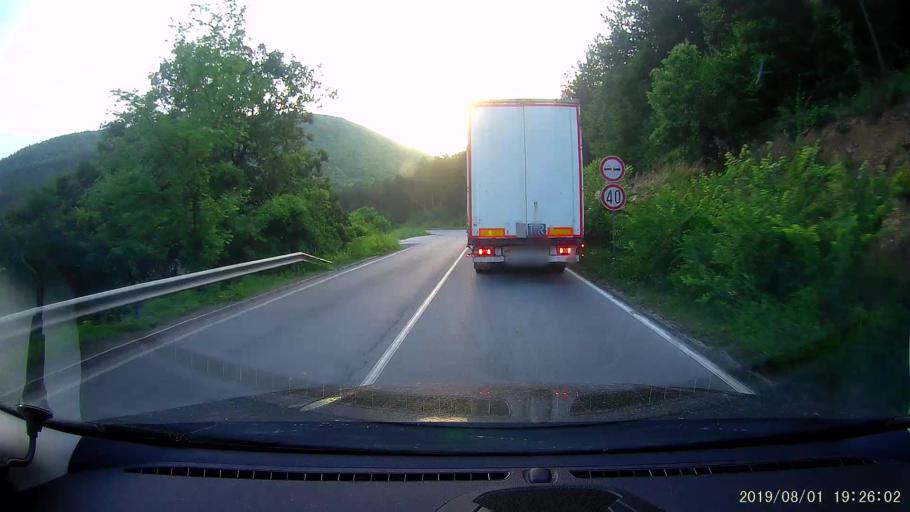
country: BG
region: Burgas
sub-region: Obshtina Sungurlare
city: Sungurlare
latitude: 42.8592
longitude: 26.9420
